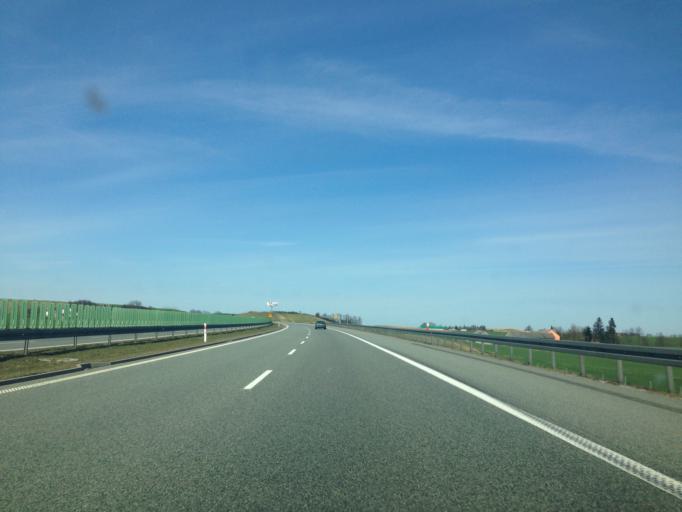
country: PL
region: Pomeranian Voivodeship
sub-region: Powiat starogardzki
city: Bobowo
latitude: 53.8579
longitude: 18.6302
